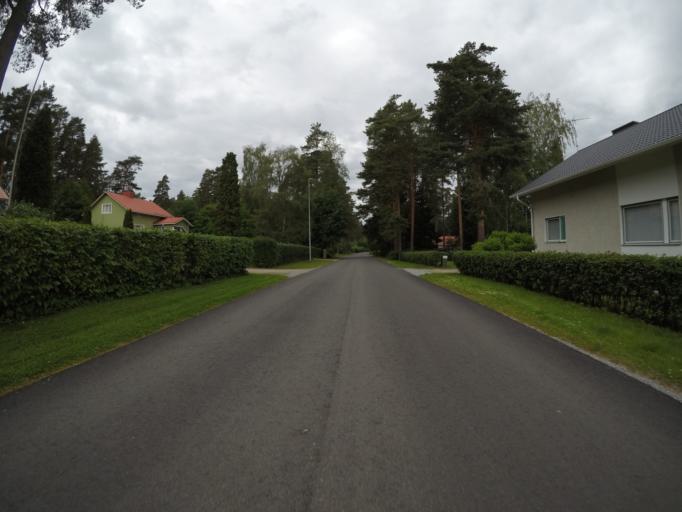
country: FI
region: Haeme
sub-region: Haemeenlinna
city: Haemeenlinna
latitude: 60.9820
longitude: 24.4597
